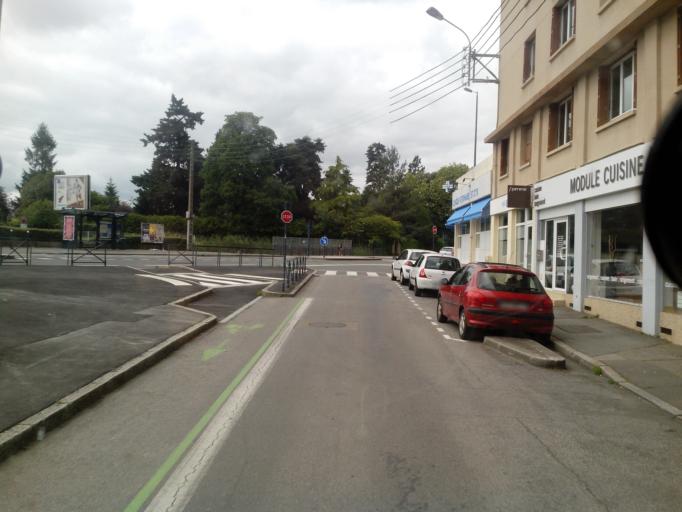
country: FR
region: Brittany
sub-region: Departement d'Ille-et-Vilaine
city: Rennes
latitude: 48.1114
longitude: -1.7005
